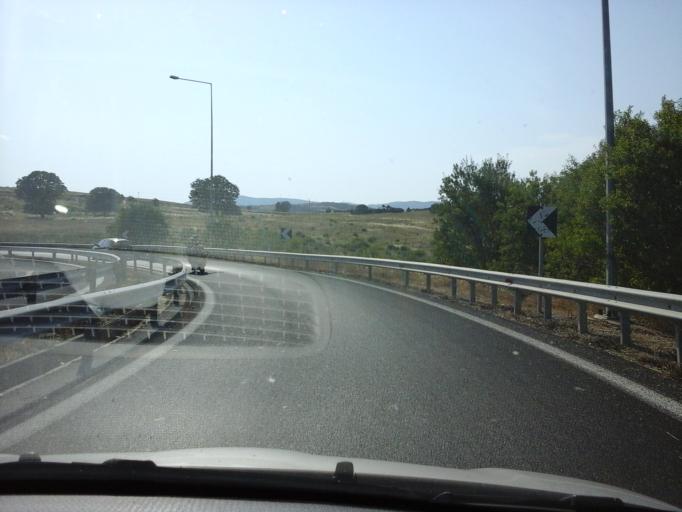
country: GR
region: East Macedonia and Thrace
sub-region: Nomos Evrou
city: Alexandroupoli
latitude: 40.8793
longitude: 25.8589
